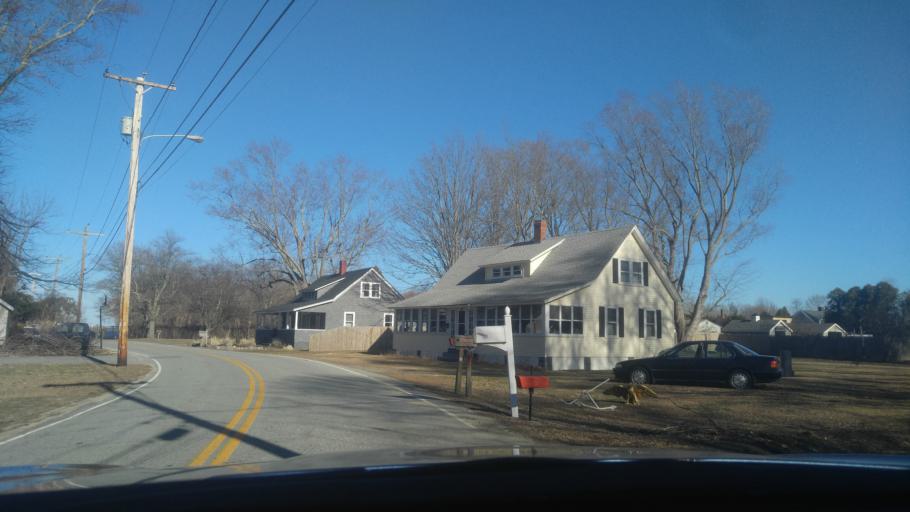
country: US
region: Rhode Island
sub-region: Kent County
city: East Greenwich
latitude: 41.6331
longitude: -71.4140
